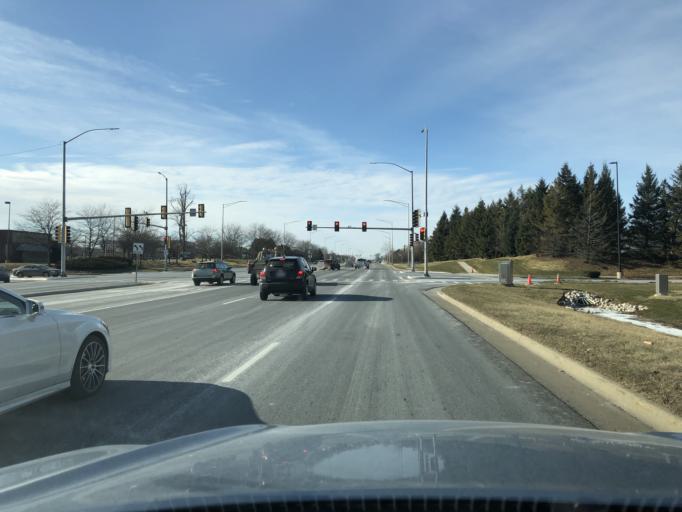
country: US
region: Illinois
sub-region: Lake County
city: Grandwood Park
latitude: 42.3855
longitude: -87.9651
